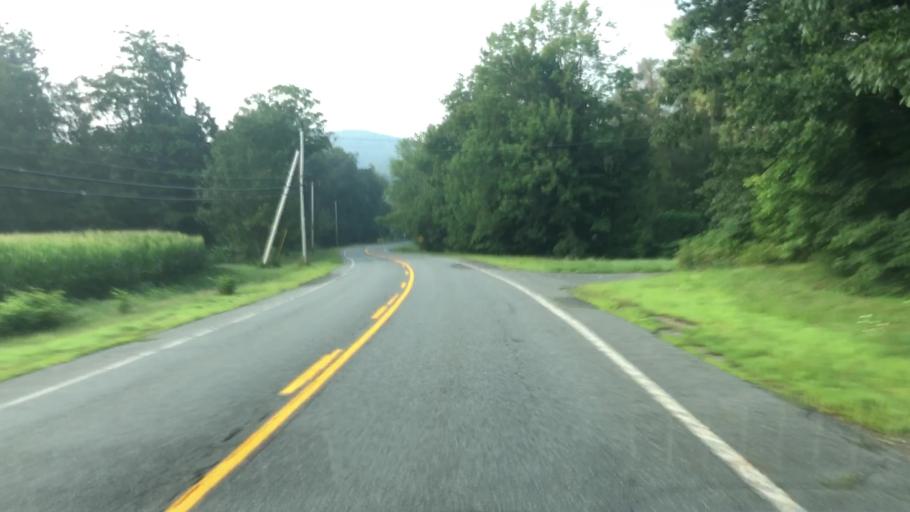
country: US
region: Massachusetts
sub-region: Franklin County
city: Buckland
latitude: 42.5706
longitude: -72.8021
